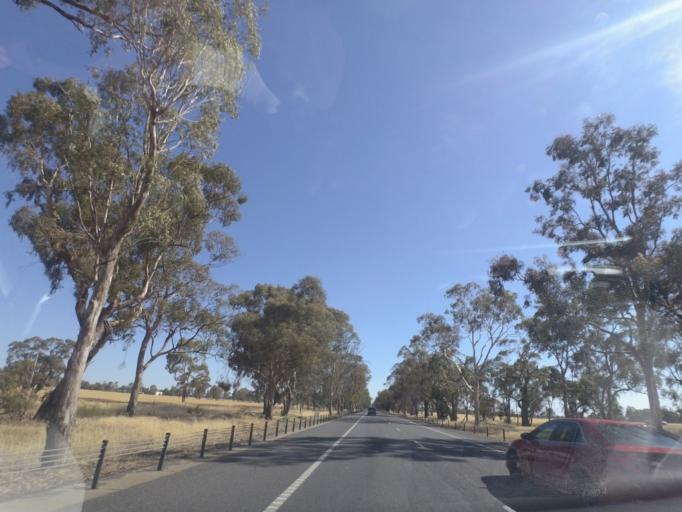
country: AU
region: Victoria
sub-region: Greater Shepparton
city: Shepparton
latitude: -36.5750
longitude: 145.3419
